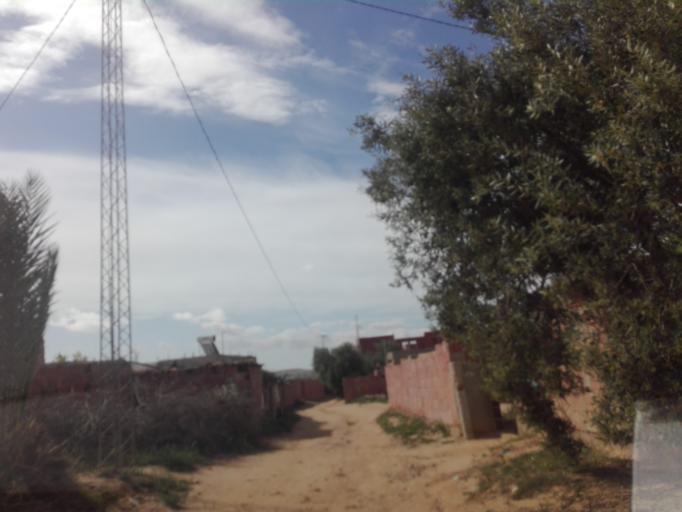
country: TN
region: Safaqis
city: Sfax
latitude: 34.7421
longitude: 10.5087
